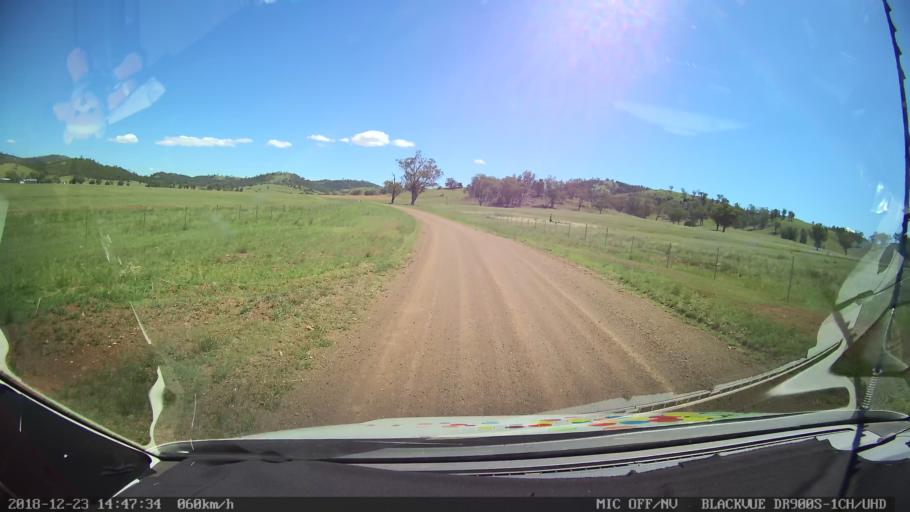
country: AU
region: New South Wales
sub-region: Tamworth Municipality
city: Manilla
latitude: -30.6548
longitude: 150.8735
